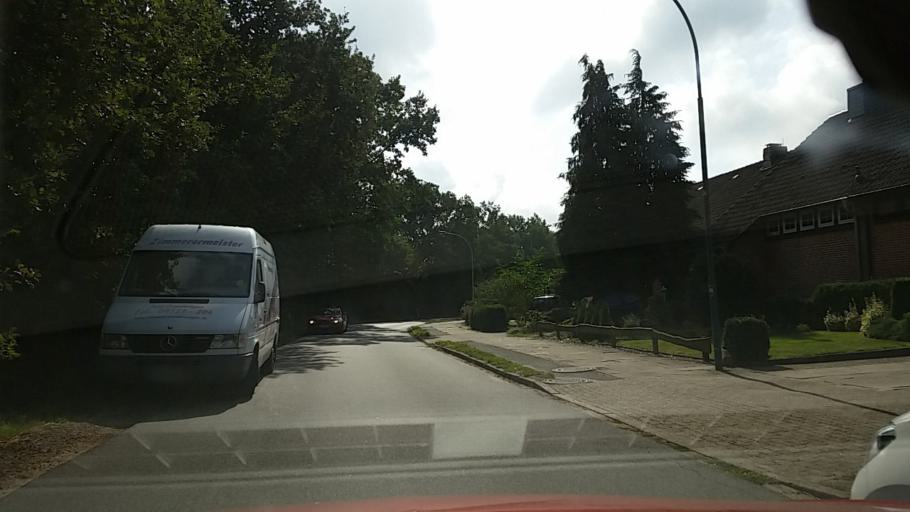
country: DE
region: Schleswig-Holstein
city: Rellingen
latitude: 53.6255
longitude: 9.7860
